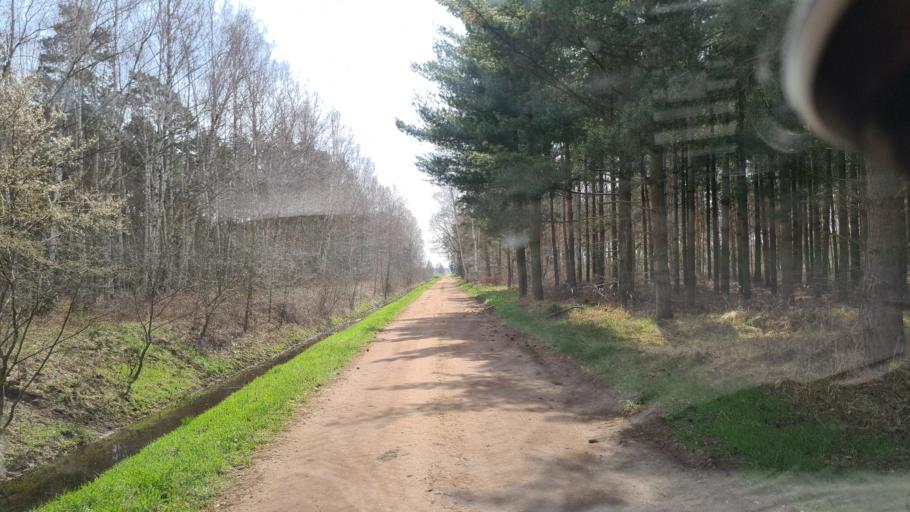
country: DE
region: Brandenburg
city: Bronkow
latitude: 51.6139
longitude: 13.9252
